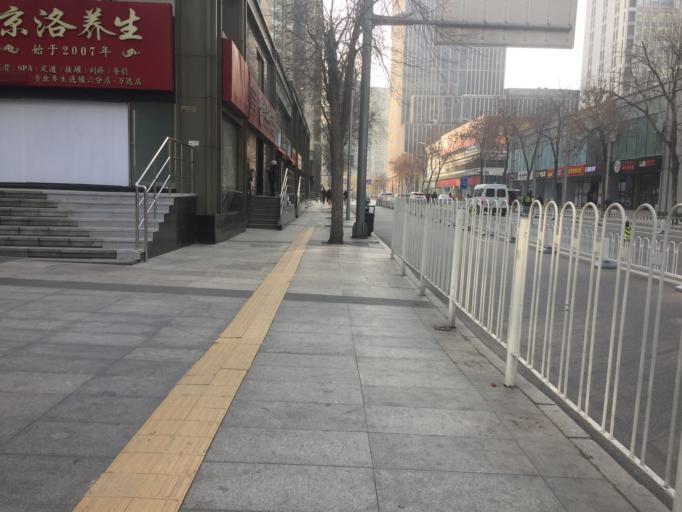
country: CN
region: Beijing
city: Chaowai
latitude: 39.9104
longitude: 116.4656
